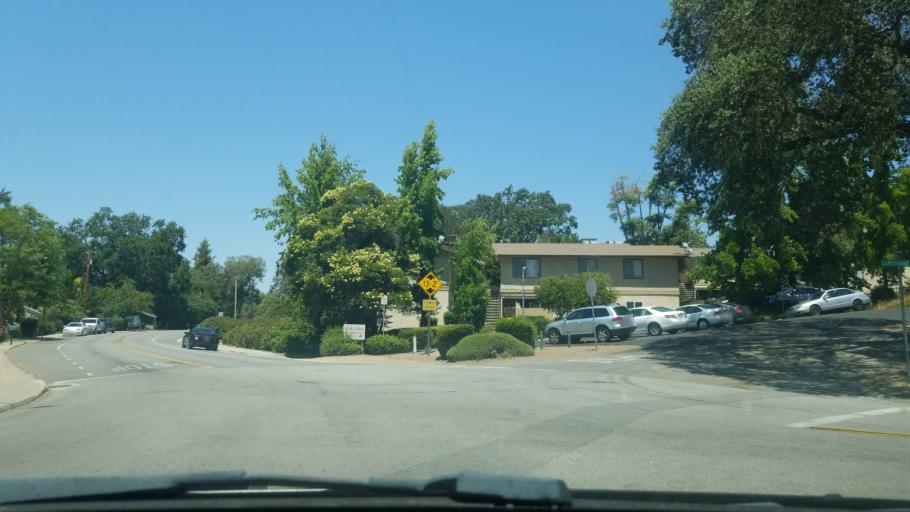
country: US
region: California
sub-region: San Luis Obispo County
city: Atascadero
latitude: 35.4933
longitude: -120.6649
